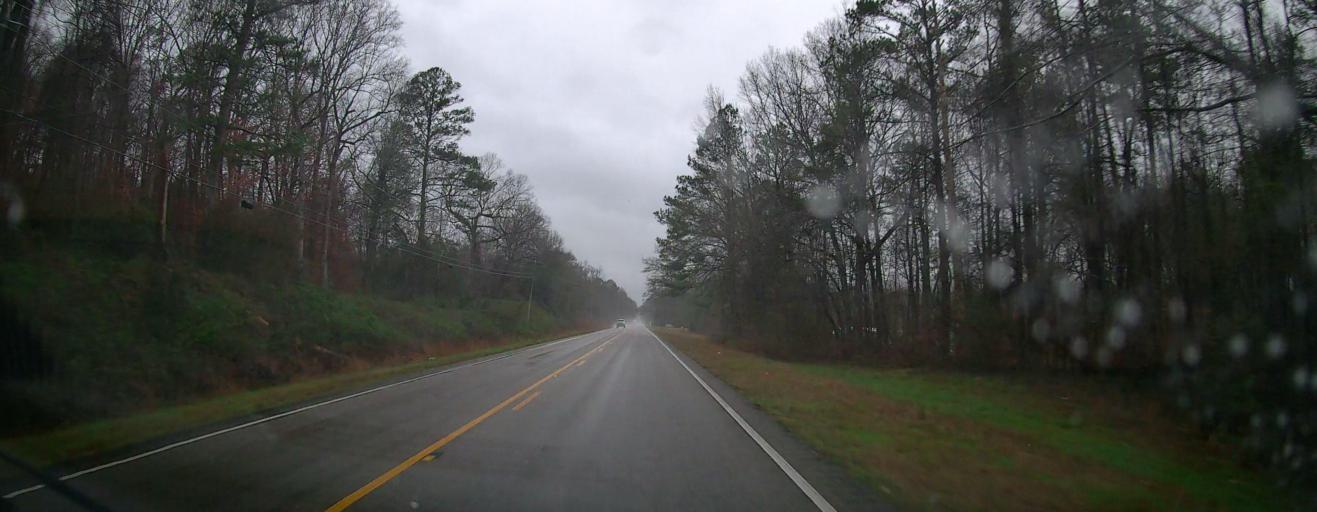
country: US
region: Alabama
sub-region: Autauga County
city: Prattville
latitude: 32.4783
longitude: -86.5272
